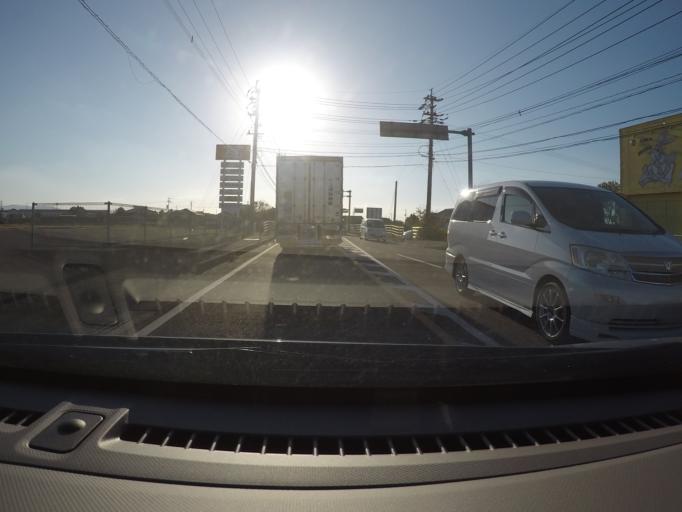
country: JP
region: Kagoshima
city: Izumi
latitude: 32.1102
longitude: 130.3269
